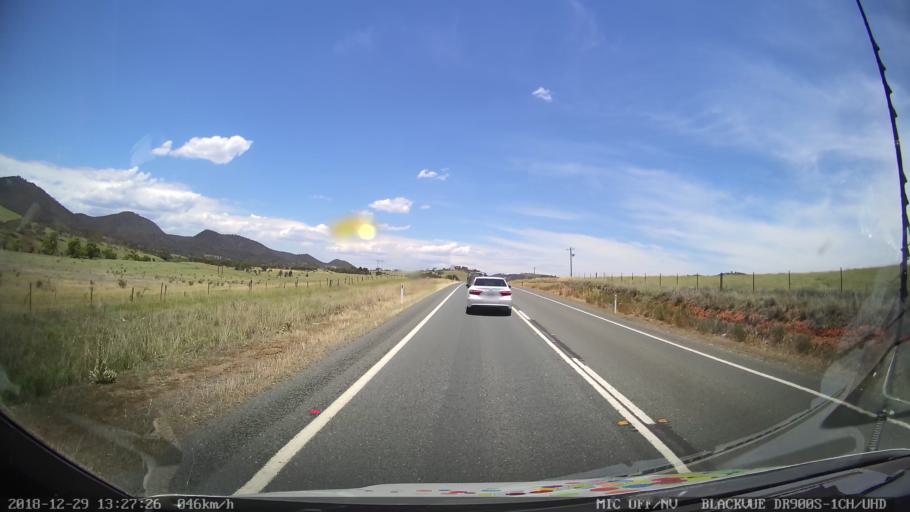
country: AU
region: New South Wales
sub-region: Cooma-Monaro
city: Cooma
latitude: -35.8661
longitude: 149.1596
